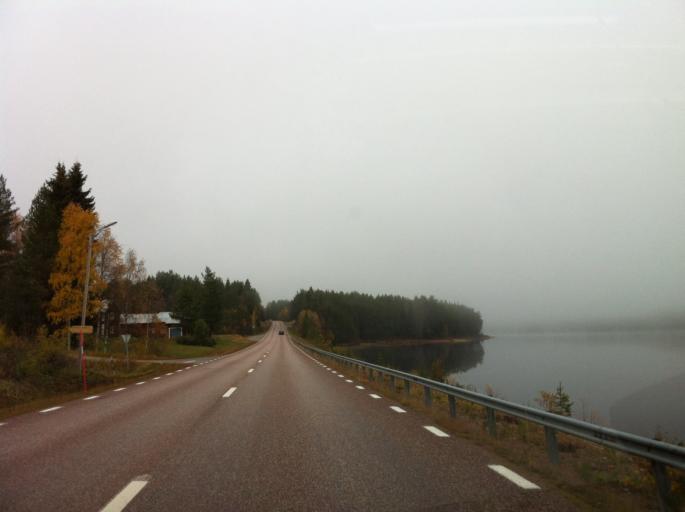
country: NO
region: Hedmark
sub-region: Trysil
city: Innbygda
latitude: 61.7410
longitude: 12.9778
